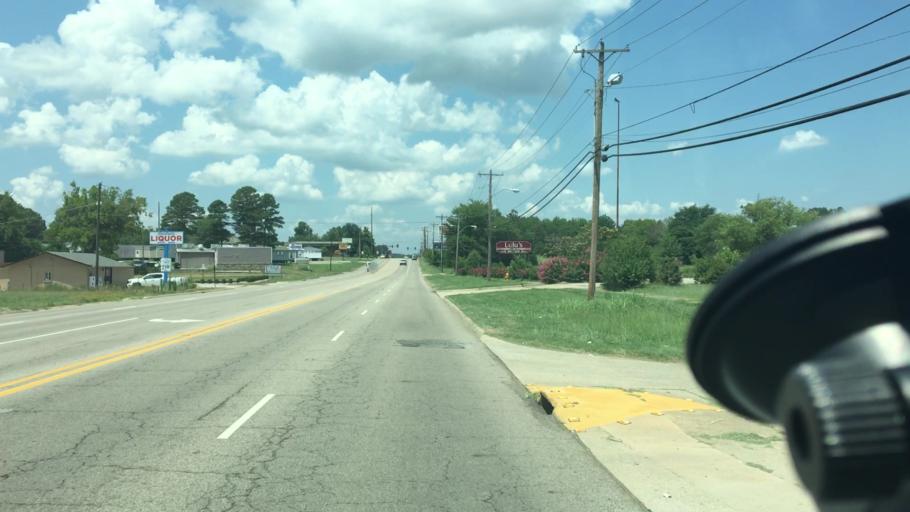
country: US
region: Arkansas
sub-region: Sebastian County
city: Barling
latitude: 35.3439
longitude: -94.3272
